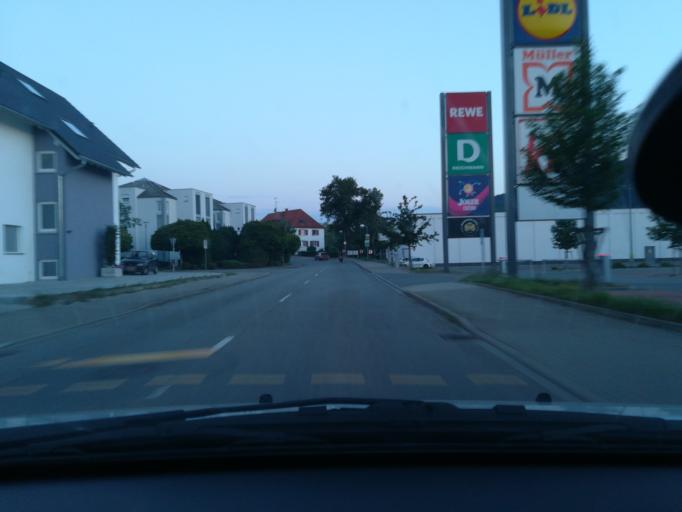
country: DE
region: Baden-Wuerttemberg
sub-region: Freiburg Region
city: Gottmadingen
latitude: 47.7362
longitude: 8.7721
